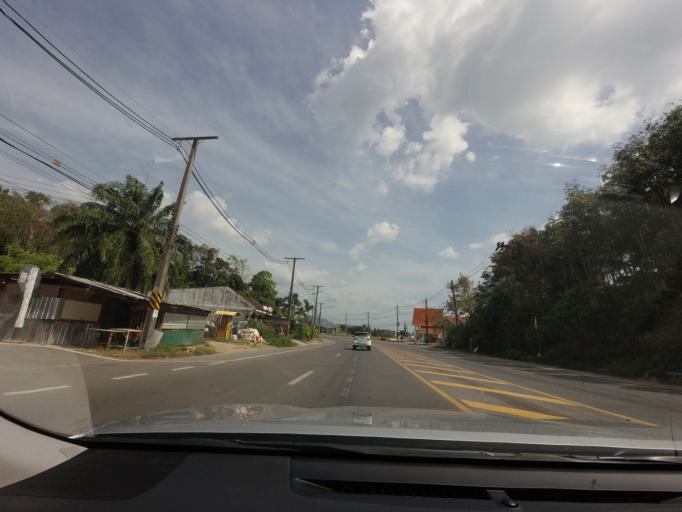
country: TH
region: Phangnga
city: Ban Ao Nang
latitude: 8.0518
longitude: 98.7717
